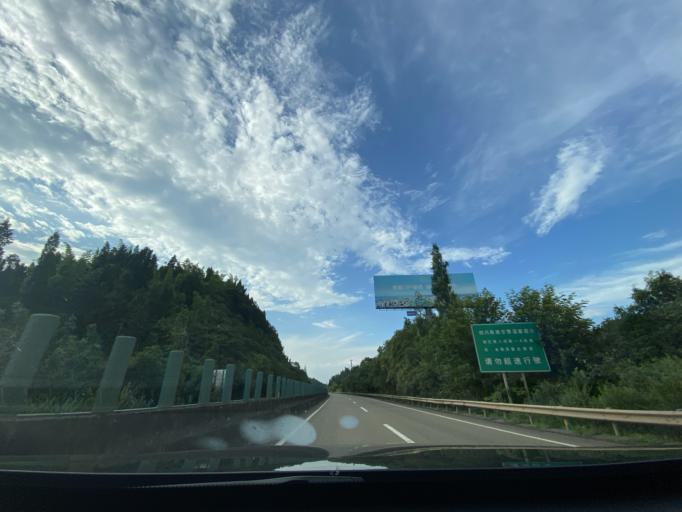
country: CN
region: Sichuan
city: Yanjiang
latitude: 30.2436
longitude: 104.6066
